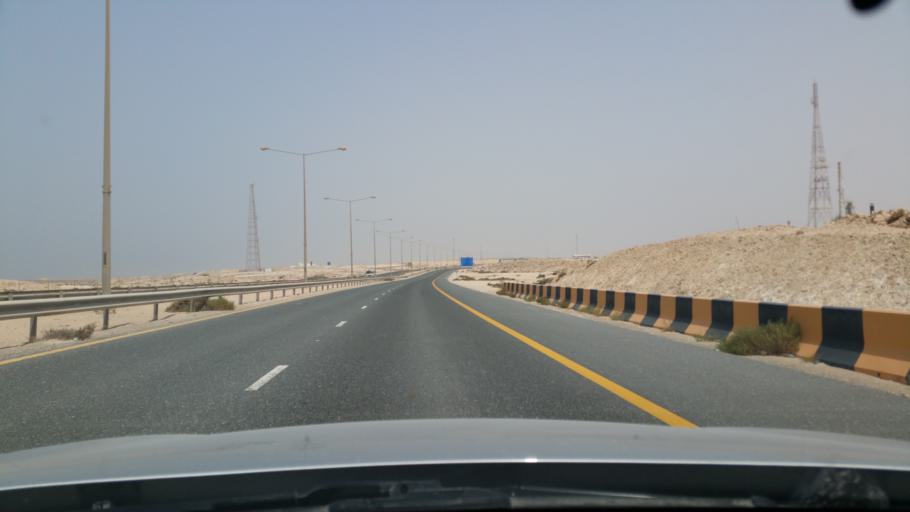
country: QA
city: Umm Bab
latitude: 25.2850
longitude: 50.7908
